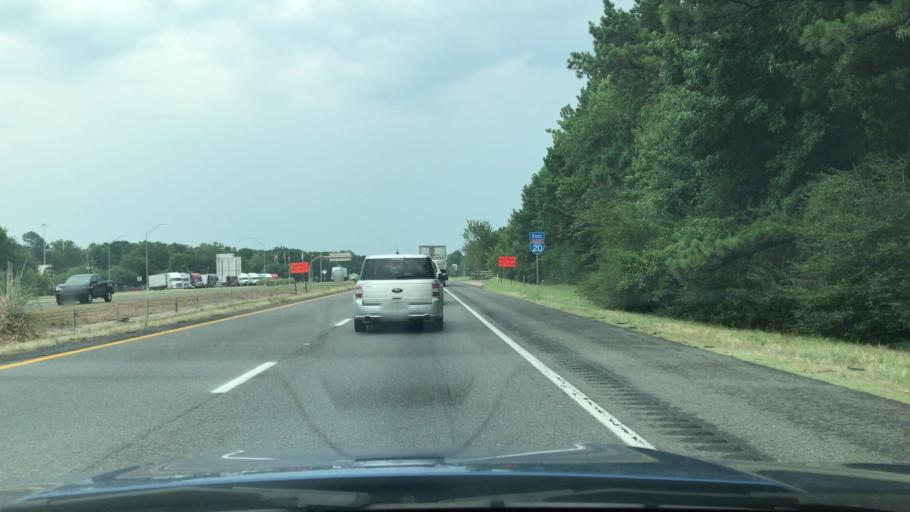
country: US
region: Texas
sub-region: Harrison County
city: Waskom
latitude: 32.4639
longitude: -94.0486
